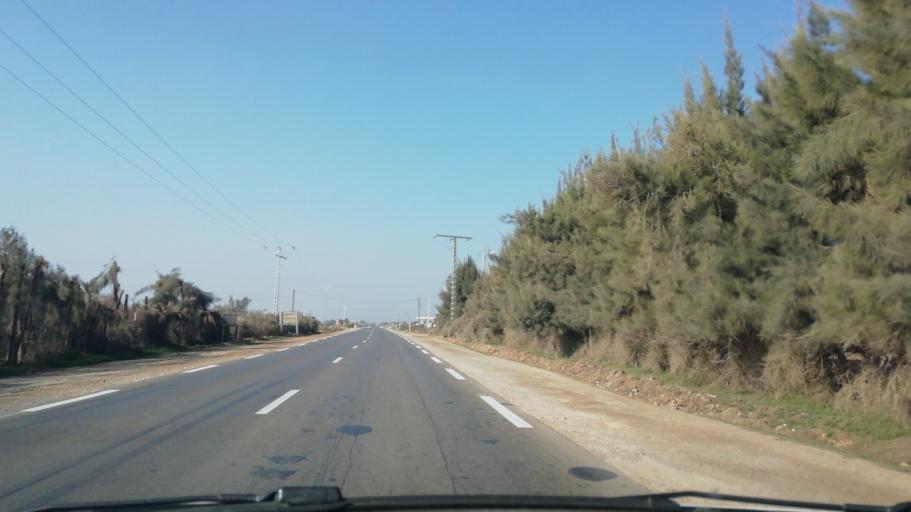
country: DZ
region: Mostaganem
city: Mostaganem
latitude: 35.7513
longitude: 0.0364
